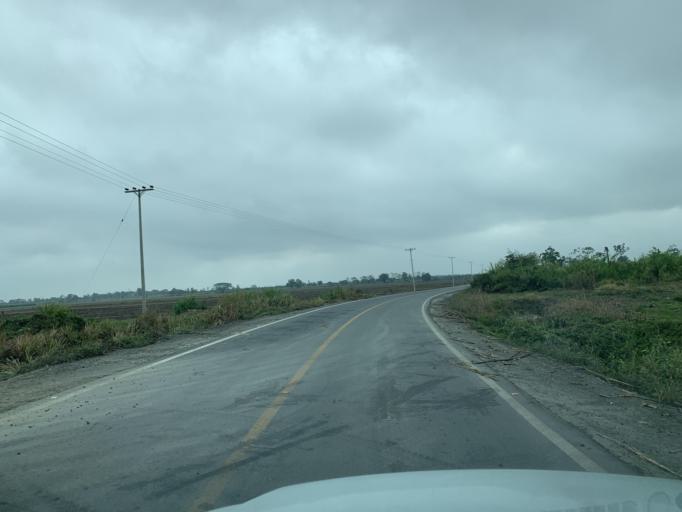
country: EC
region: Guayas
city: Coronel Marcelino Mariduena
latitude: -2.3083
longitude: -79.5091
